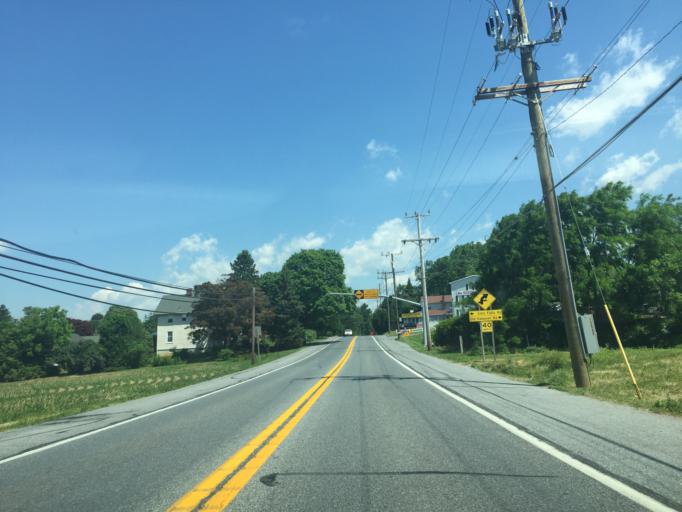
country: US
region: Maryland
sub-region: Baltimore County
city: Reisterstown
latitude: 39.5035
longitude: -76.8335
